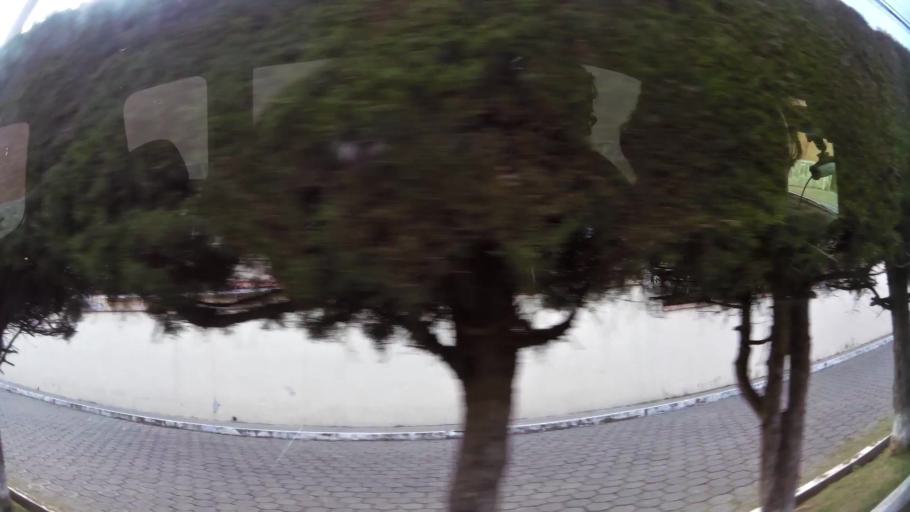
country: GT
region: Quetzaltenango
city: Quetzaltenango
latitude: 14.8490
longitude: -91.5414
